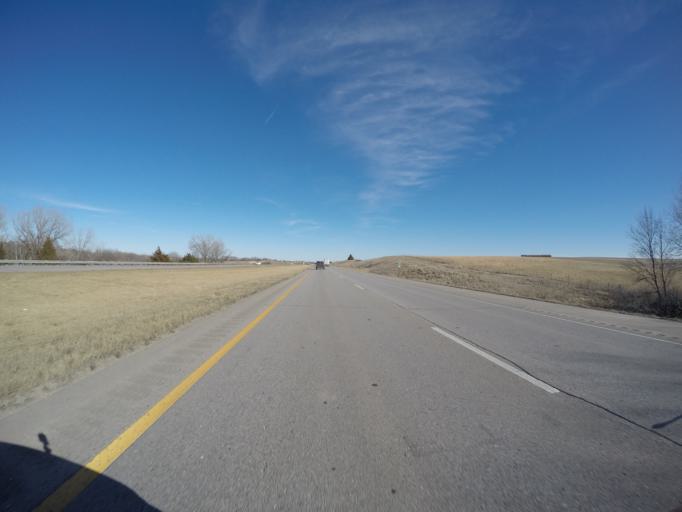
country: US
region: Nebraska
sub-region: Seward County
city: Milford
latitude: 40.8212
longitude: -96.9673
